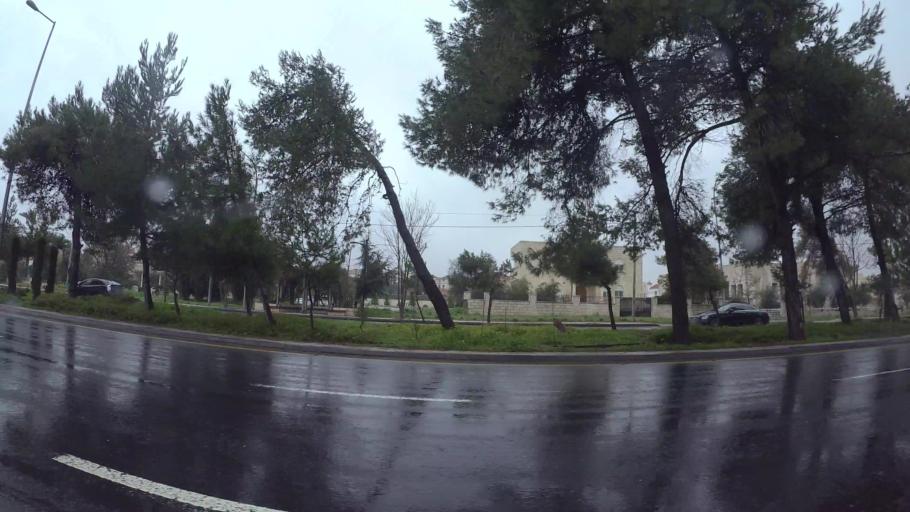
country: JO
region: Amman
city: Wadi as Sir
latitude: 31.9933
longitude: 35.8237
